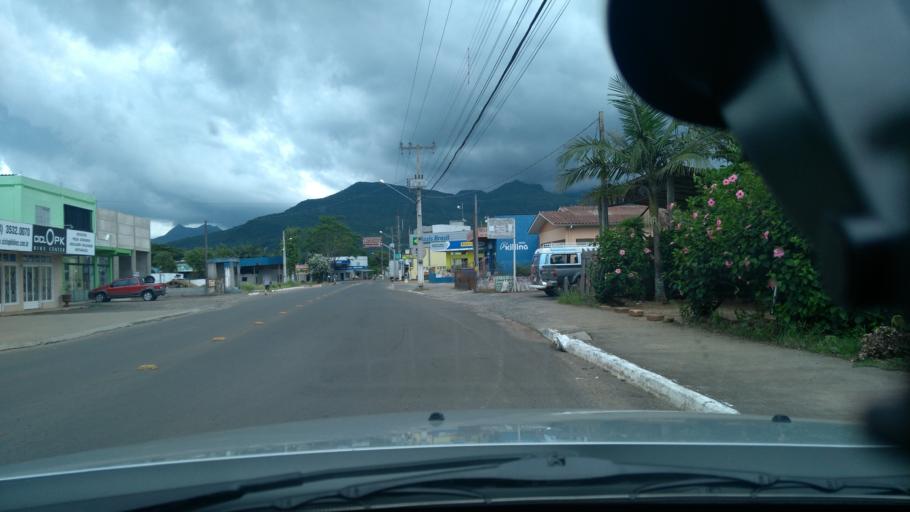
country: BR
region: Rio Grande do Sul
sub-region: Torres
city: Torres
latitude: -29.1952
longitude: -49.9458
